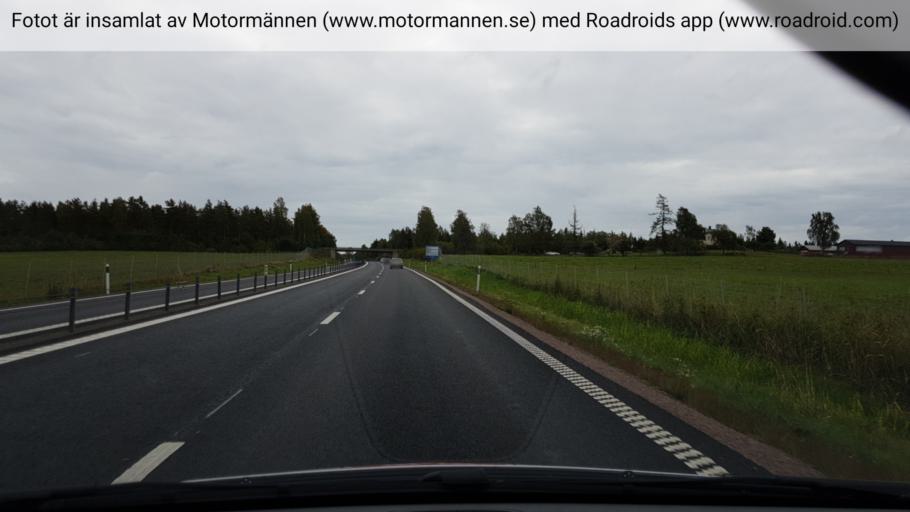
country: SE
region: Vaermland
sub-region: Karlstads Kommun
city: Skattkarr
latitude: 59.3942
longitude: 13.8184
